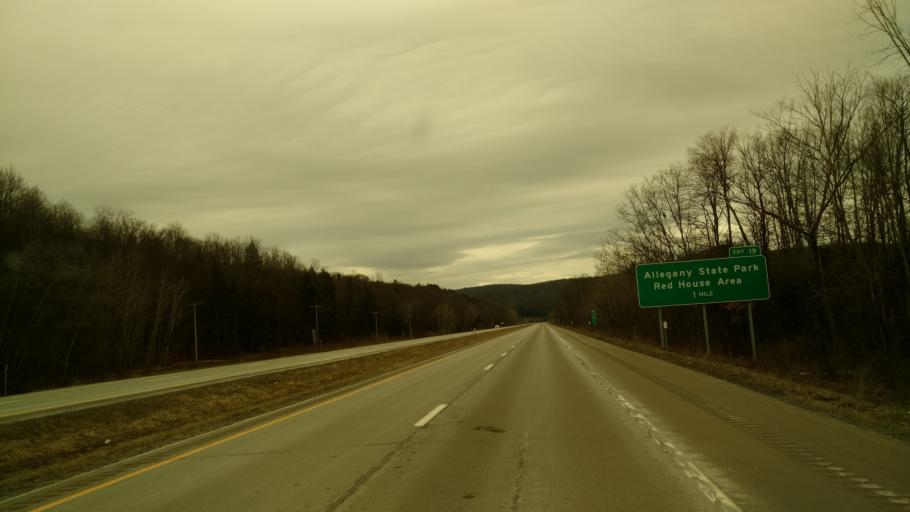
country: US
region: New York
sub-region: Cattaraugus County
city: Salamanca
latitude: 42.1235
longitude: -78.7788
